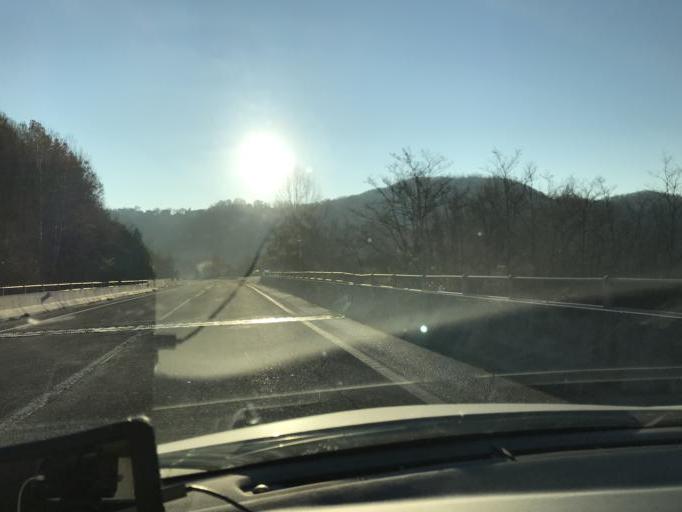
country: IT
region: Latium
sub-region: Provincia di Rieti
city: Fiamignano
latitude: 42.2564
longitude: 13.1360
